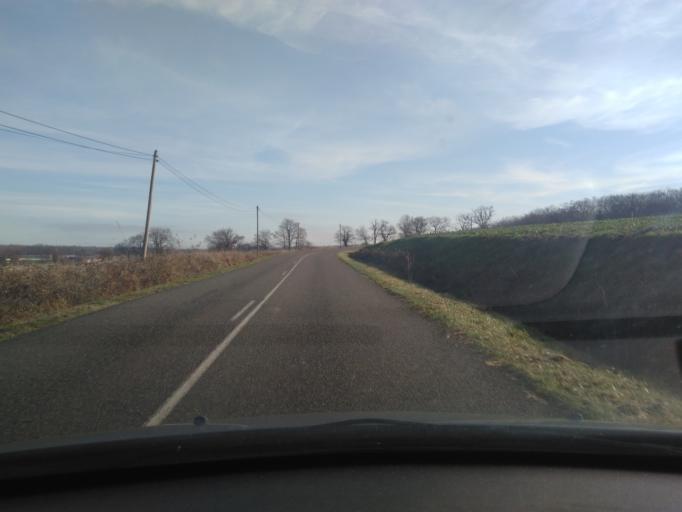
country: FR
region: Bourgogne
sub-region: Departement de la Nievre
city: Saint-Parize-le-Chatel
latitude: 46.8120
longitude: 3.2619
